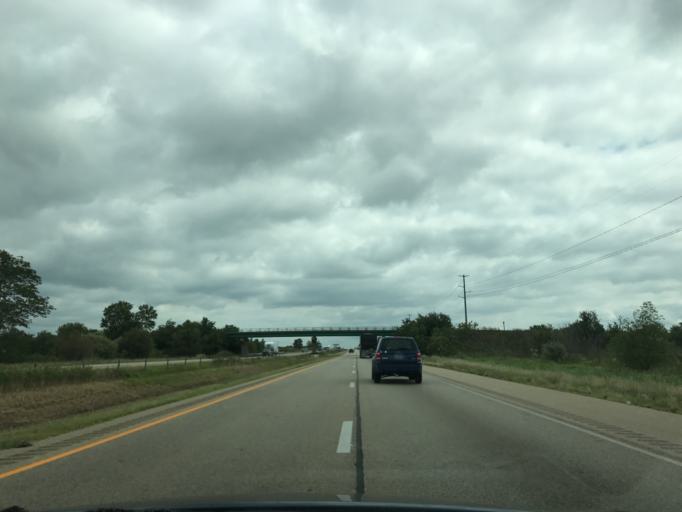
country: US
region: Illinois
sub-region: LaSalle County
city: Deer Park
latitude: 41.3678
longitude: -88.9740
